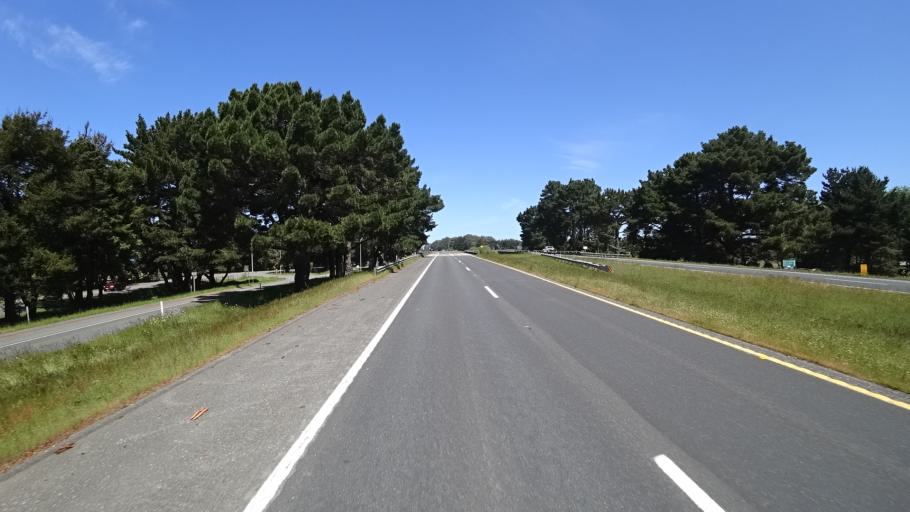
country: US
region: California
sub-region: Humboldt County
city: McKinleyville
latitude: 40.9681
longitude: -124.1161
